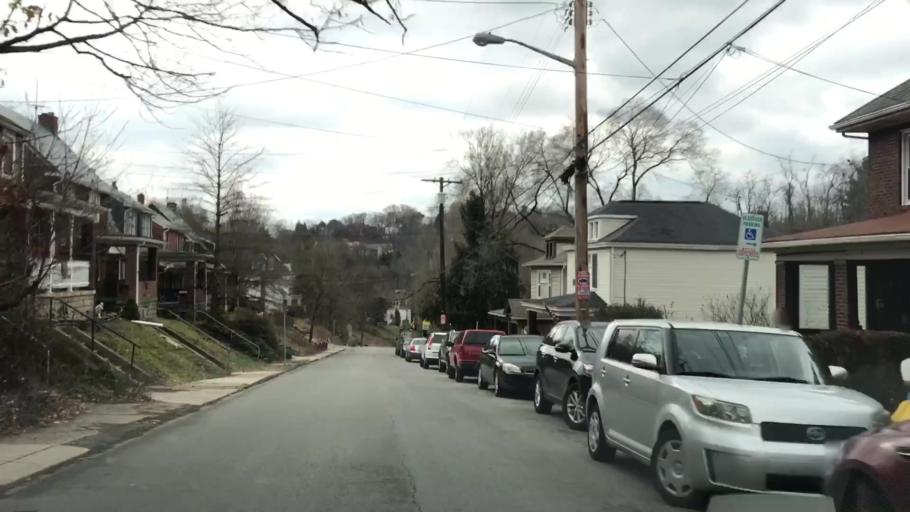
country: US
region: Pennsylvania
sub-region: Allegheny County
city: Crafton
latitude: 40.4408
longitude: -80.0513
